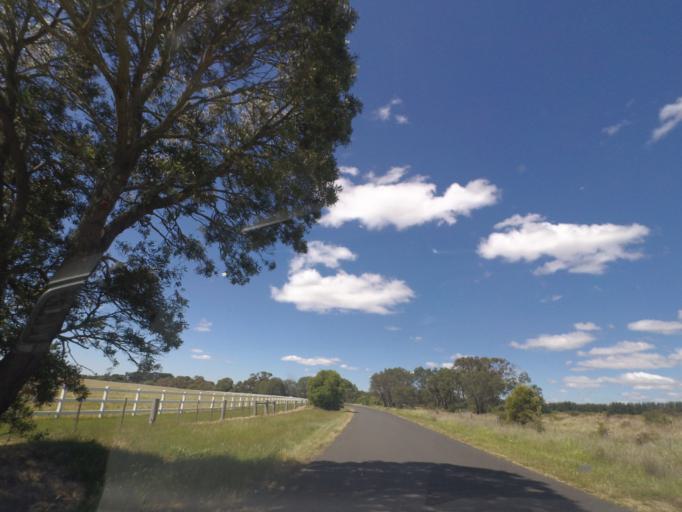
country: AU
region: Victoria
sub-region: Moorabool
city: Bacchus Marsh
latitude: -37.3355
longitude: 144.4409
